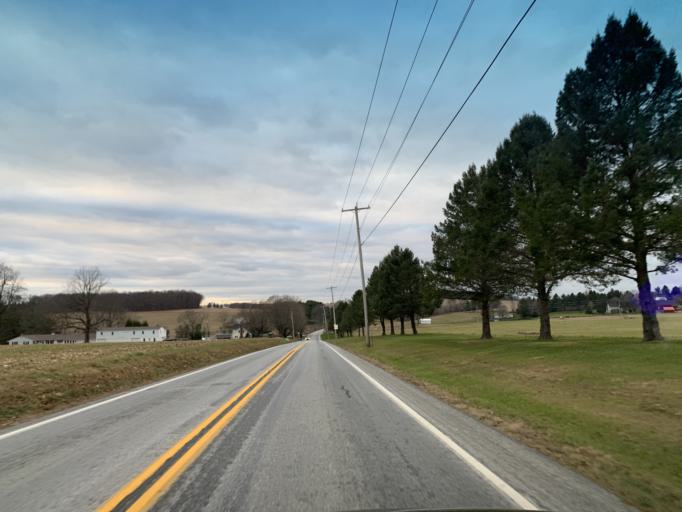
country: US
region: Pennsylvania
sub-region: York County
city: Stewartstown
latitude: 39.7800
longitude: -76.6130
